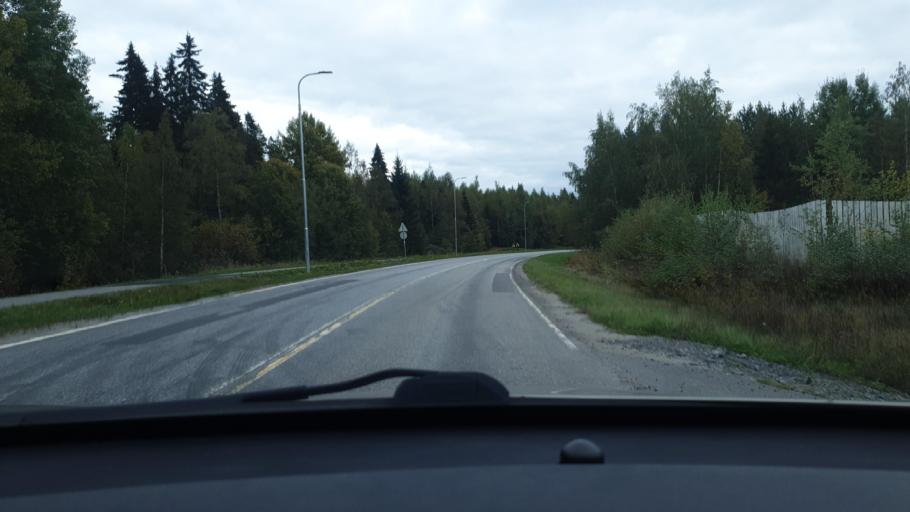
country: FI
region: Ostrobothnia
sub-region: Vaasa
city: Teeriniemi
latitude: 63.0694
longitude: 21.7043
